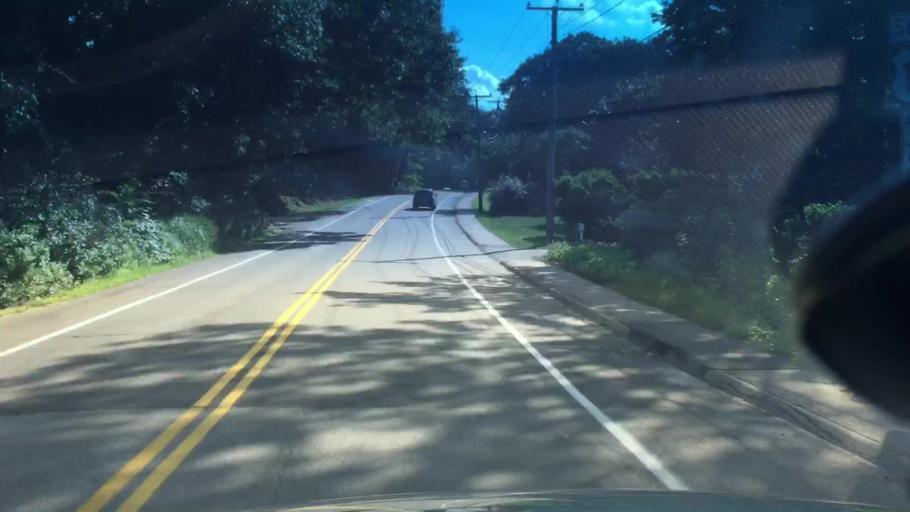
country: US
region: Maine
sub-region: York County
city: York Harbor
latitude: 43.1505
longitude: -70.6249
